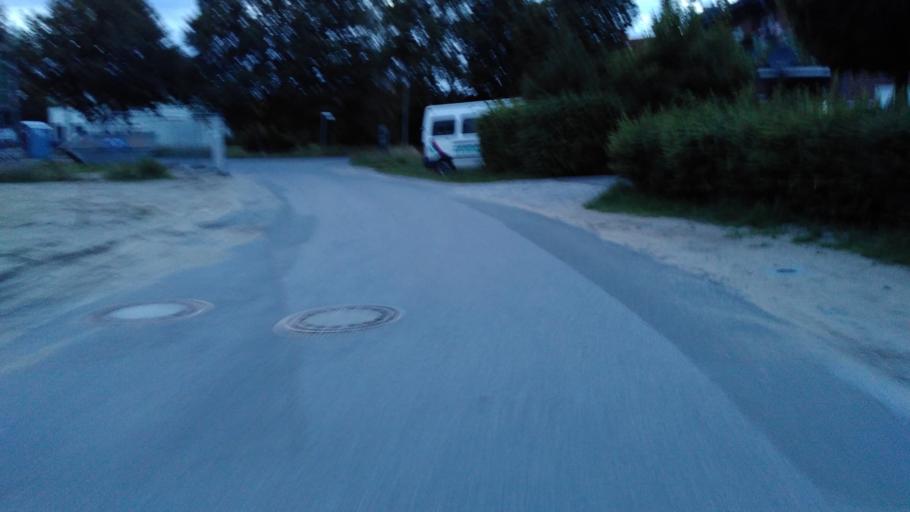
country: DE
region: North Rhine-Westphalia
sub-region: Regierungsbezirk Detmold
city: Verl
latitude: 51.8726
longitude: 8.4963
